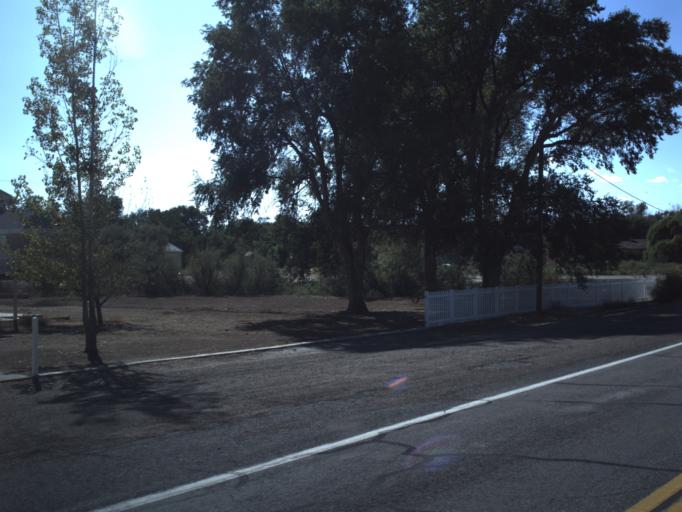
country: US
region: Utah
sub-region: Millard County
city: Delta
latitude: 39.2887
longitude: -112.6527
